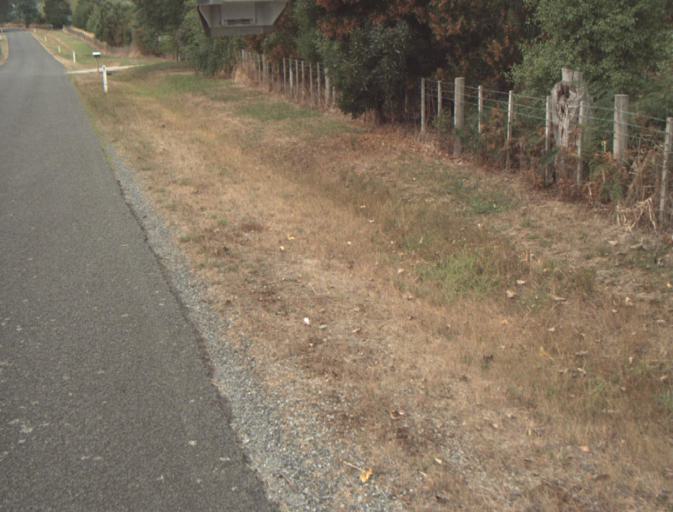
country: AU
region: Tasmania
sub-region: Launceston
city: Mayfield
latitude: -41.2941
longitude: 146.9904
